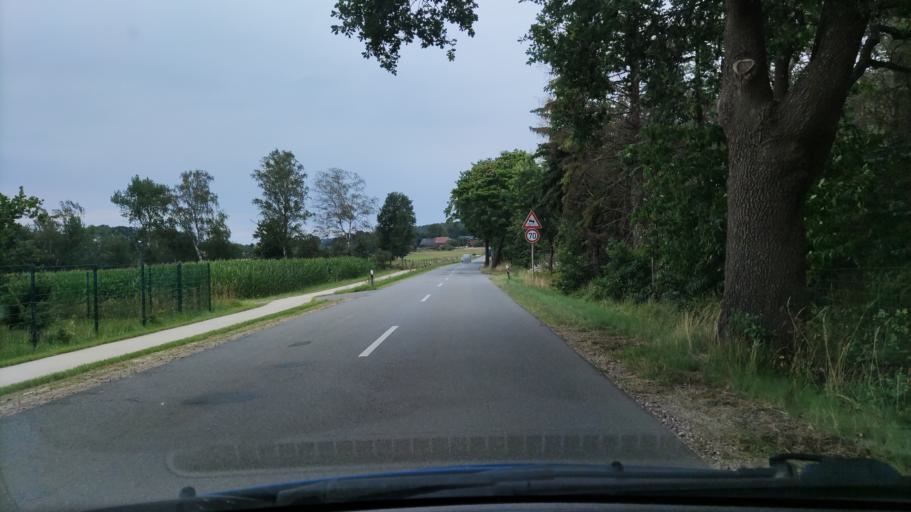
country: DE
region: Lower Saxony
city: Rosche
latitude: 52.9958
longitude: 10.7665
